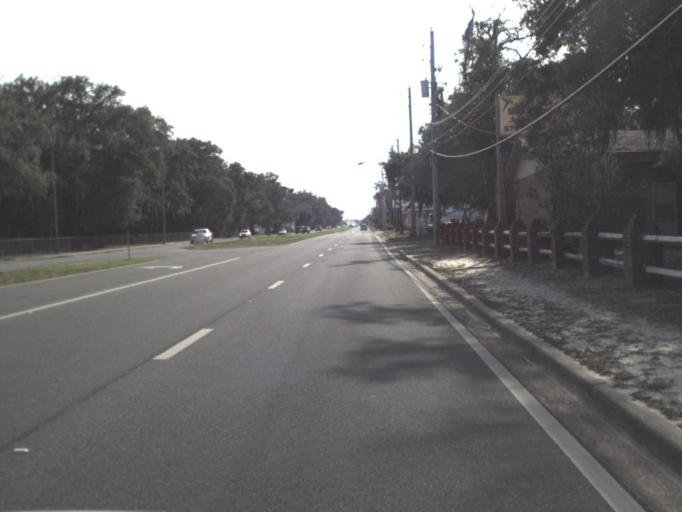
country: US
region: Florida
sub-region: Bay County
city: Parker
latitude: 30.1197
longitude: -85.5946
